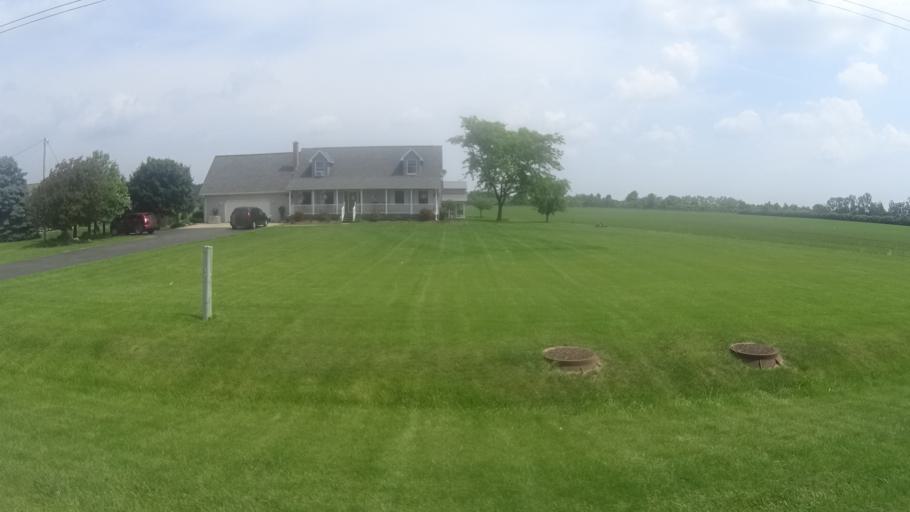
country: US
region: Ohio
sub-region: Erie County
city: Milan
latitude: 41.3364
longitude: -82.6536
